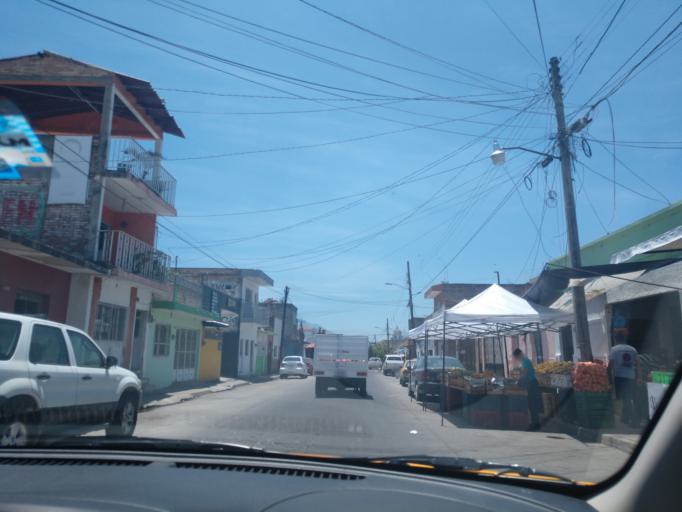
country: MX
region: Nayarit
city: Tepic
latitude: 21.5180
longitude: -104.9015
